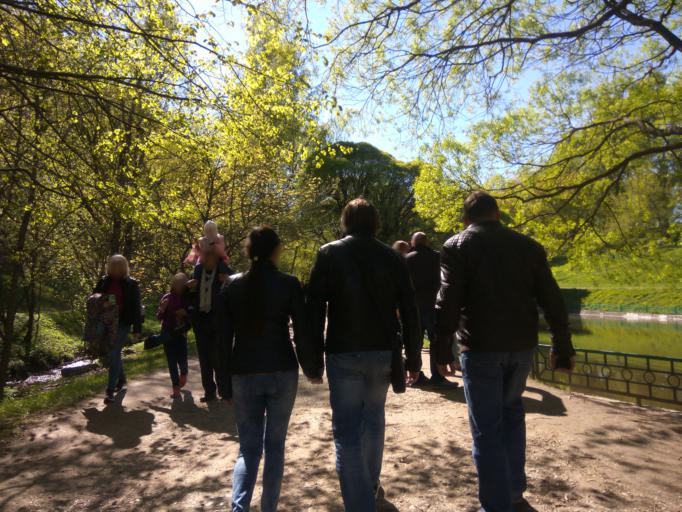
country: RU
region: Moscow
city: Kolomenskoye
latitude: 55.6652
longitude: 37.6703
